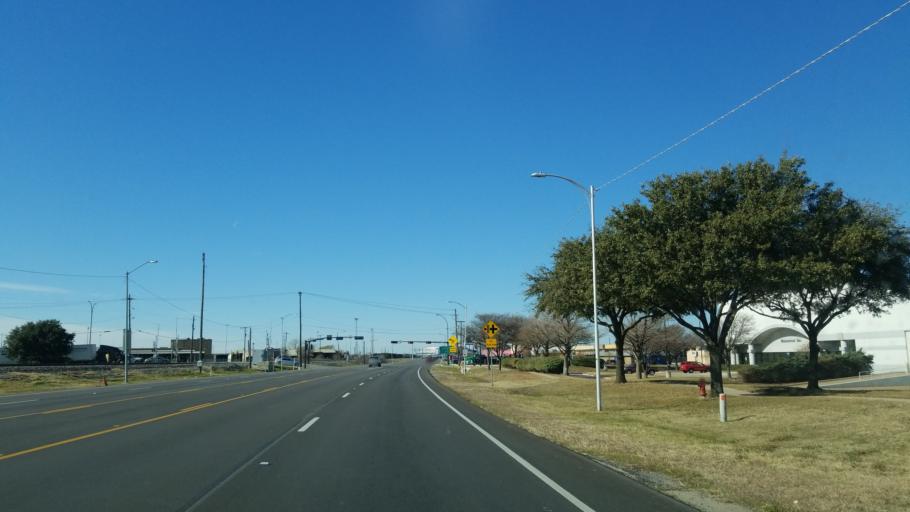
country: US
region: Texas
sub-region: Dallas County
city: Grand Prairie
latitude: 32.7393
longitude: -97.0443
